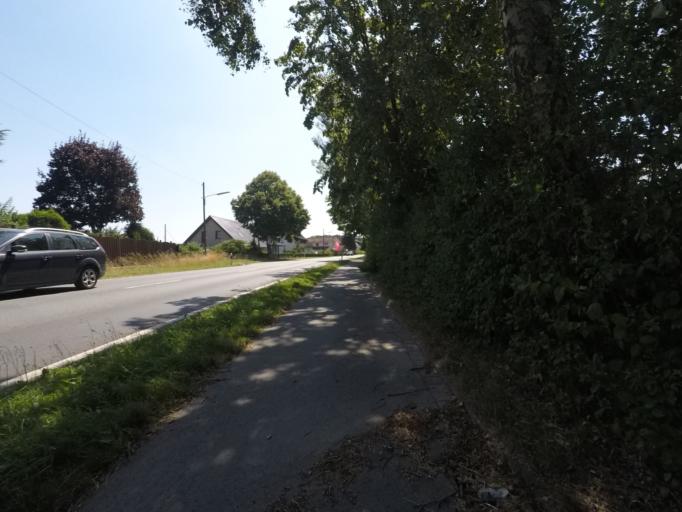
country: DE
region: North Rhine-Westphalia
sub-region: Regierungsbezirk Detmold
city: Hiddenhausen
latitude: 52.1387
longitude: 8.6232
